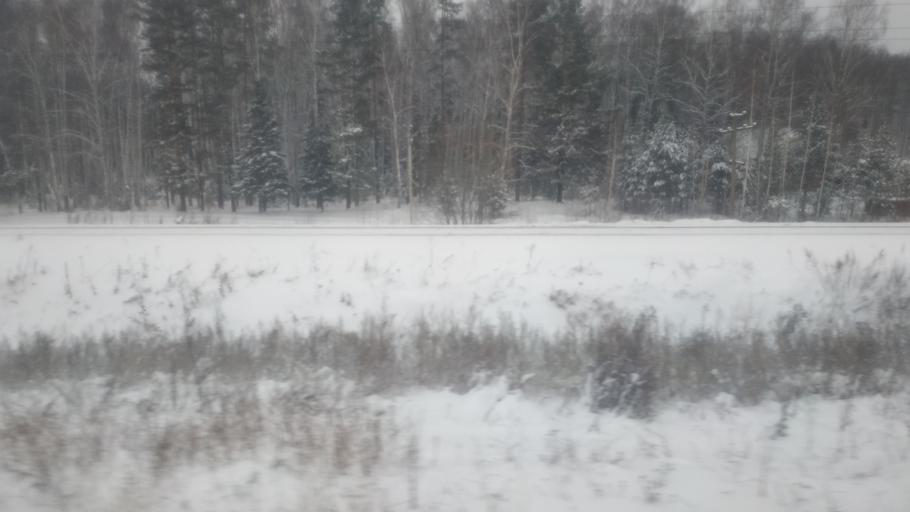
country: RU
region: Udmurtiya
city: Malaya Purga
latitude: 56.5545
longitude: 53.1076
